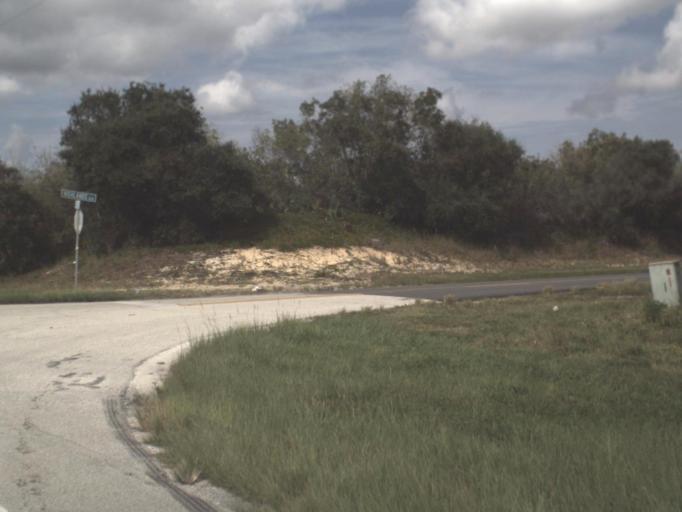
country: US
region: Florida
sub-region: Highlands County
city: Lake Placid
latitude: 27.2083
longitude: -81.3079
